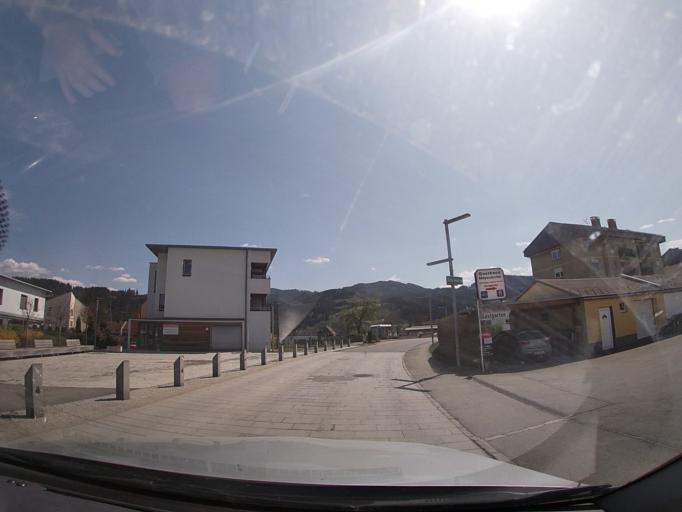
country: AT
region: Styria
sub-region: Politischer Bezirk Murtal
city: Apfelberg
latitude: 47.2060
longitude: 14.8341
